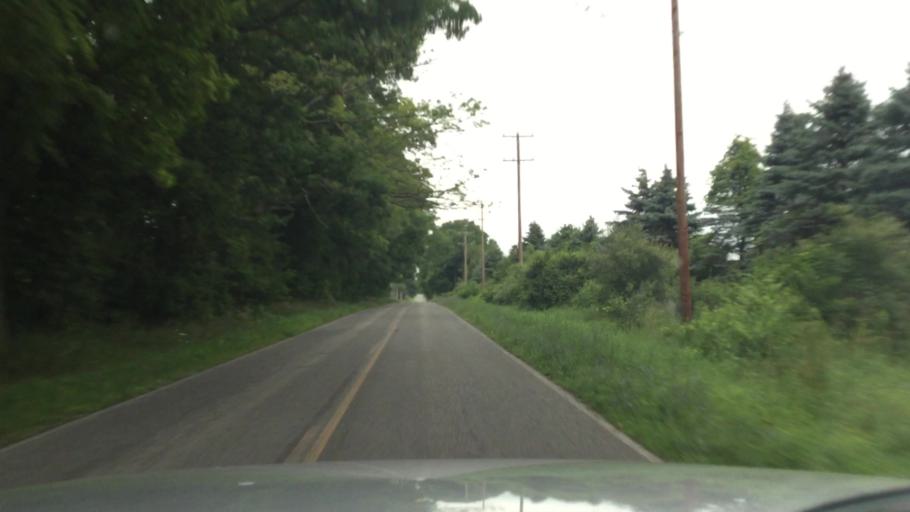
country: US
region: Michigan
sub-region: Montcalm County
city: Greenville
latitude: 43.1792
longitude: -85.2233
